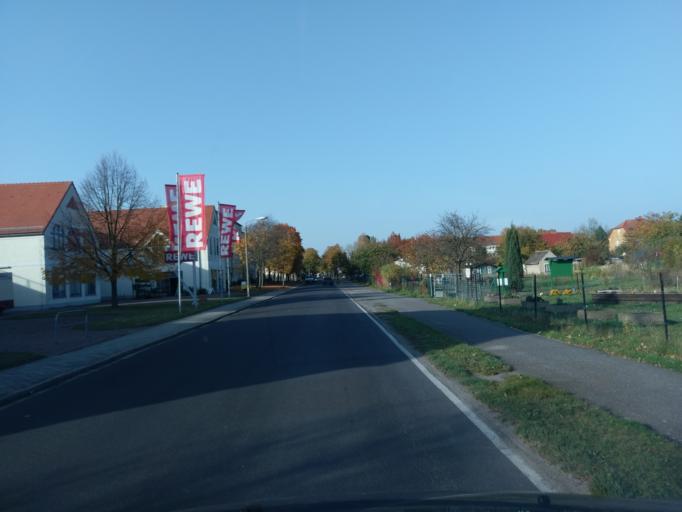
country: DE
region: Brandenburg
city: Falkenberg
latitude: 51.5768
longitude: 13.2447
